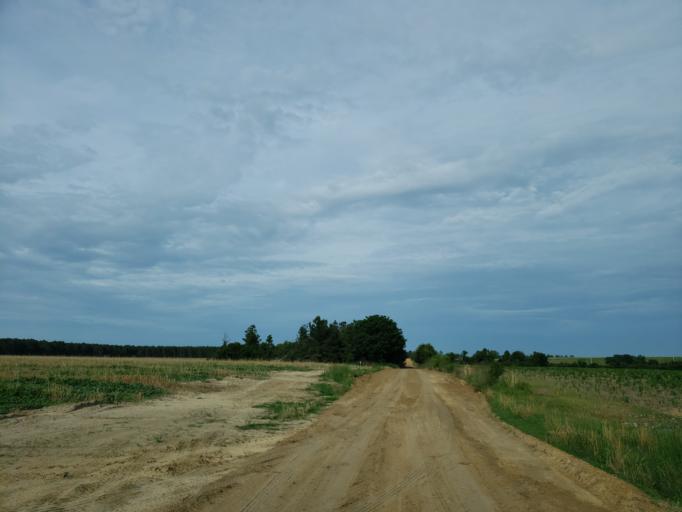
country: US
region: Georgia
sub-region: Dooly County
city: Vienna
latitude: 32.1279
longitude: -83.7714
